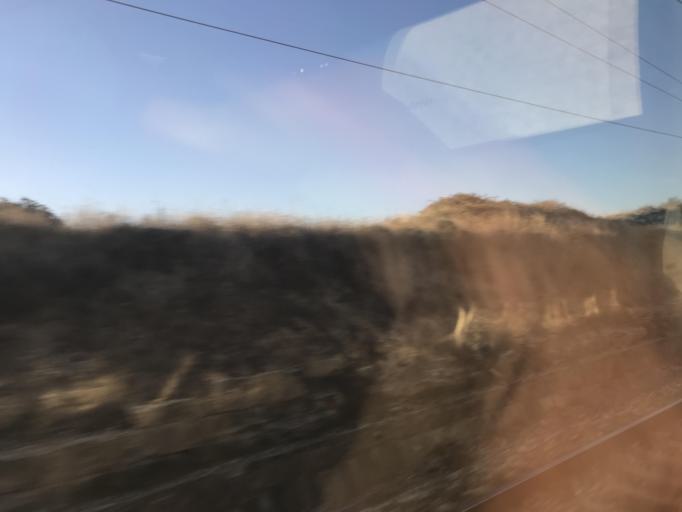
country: ES
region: Basque Country
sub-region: Provincia de Alava
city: Gasteiz / Vitoria
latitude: 42.8403
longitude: -2.7733
